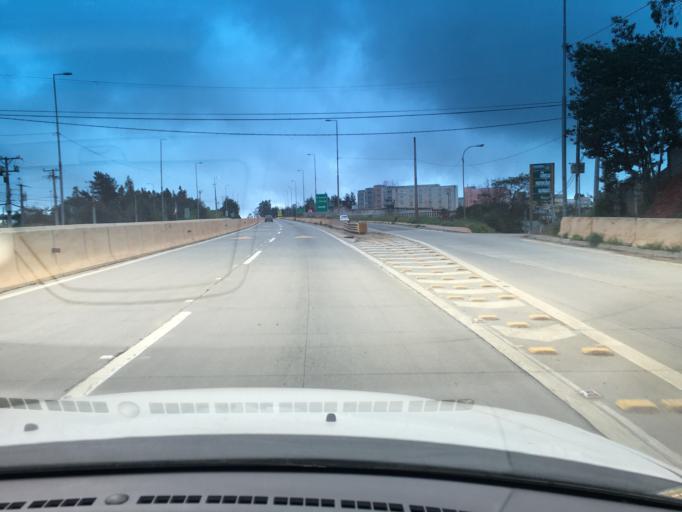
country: CL
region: Valparaiso
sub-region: Provincia de Valparaiso
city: Valparaiso
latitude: -33.0692
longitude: -71.6307
